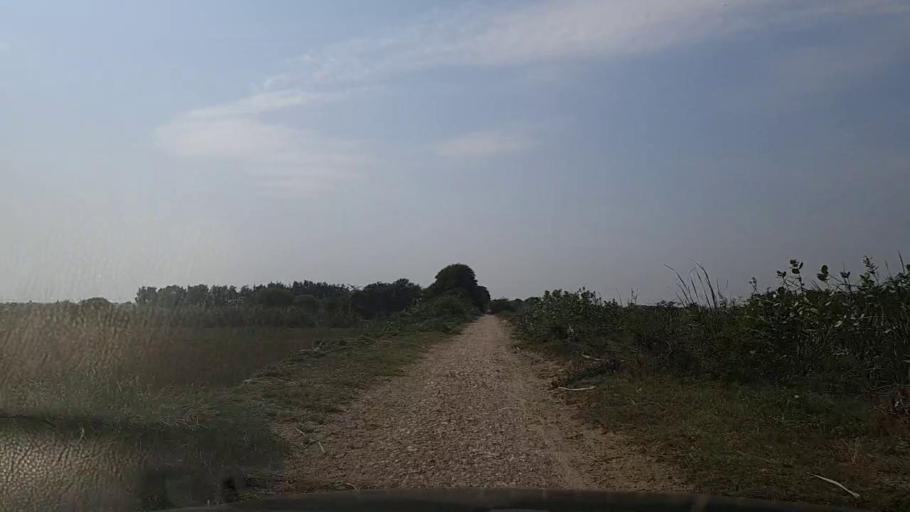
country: PK
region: Sindh
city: Thatta
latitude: 24.7661
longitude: 67.7954
